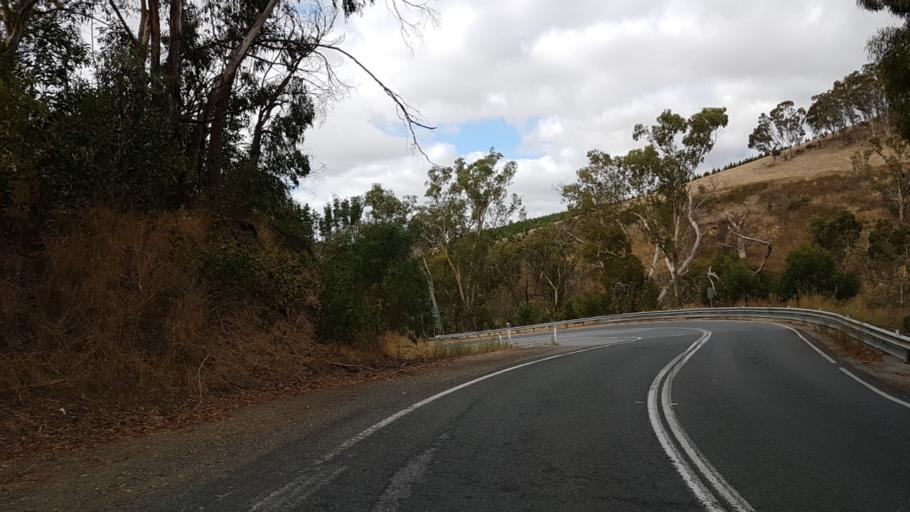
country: AU
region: South Australia
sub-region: Adelaide Hills
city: Gumeracha
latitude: -34.8236
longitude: 138.8516
